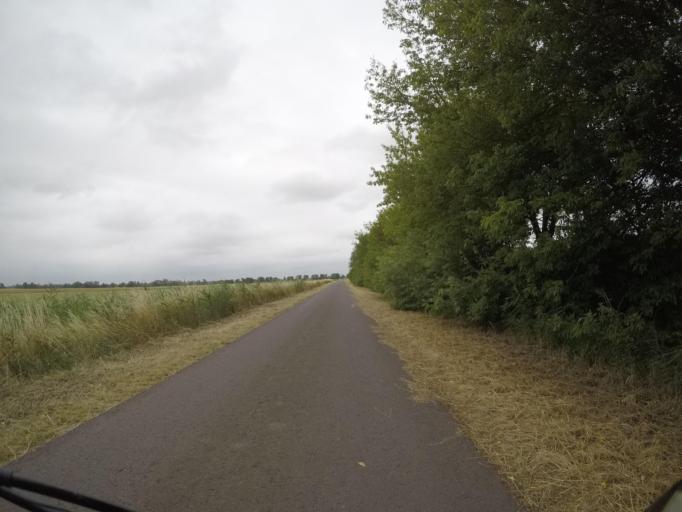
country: DE
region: Lower Saxony
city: Hitzacker
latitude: 53.1728
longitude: 11.0894
